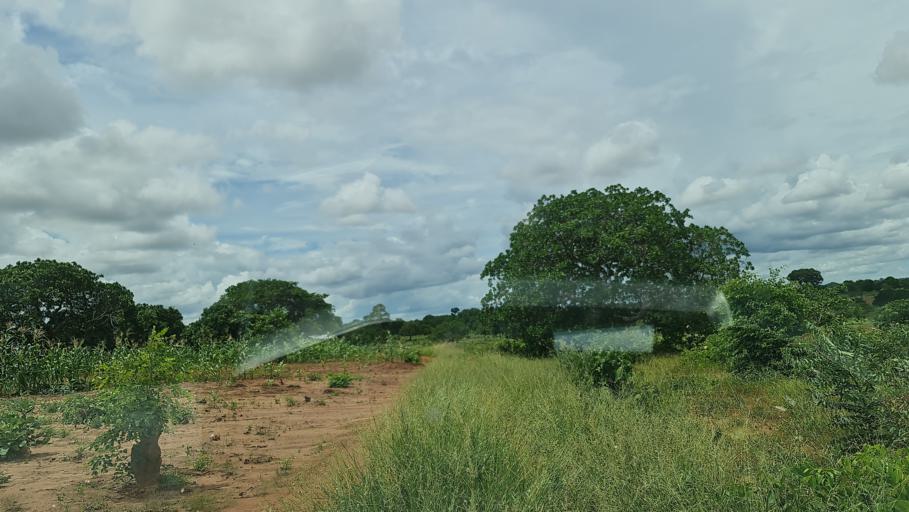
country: MZ
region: Nampula
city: Nacala
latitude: -14.7836
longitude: 39.9814
